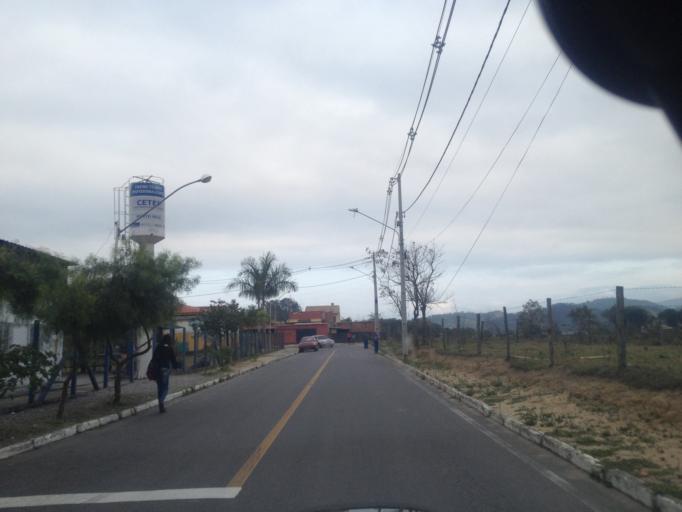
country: BR
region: Rio de Janeiro
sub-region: Porto Real
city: Porto Real
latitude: -22.4130
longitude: -44.3054
